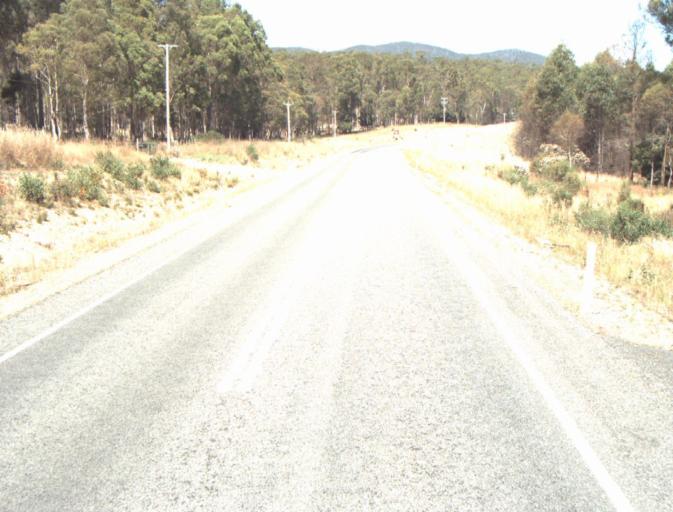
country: AU
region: Tasmania
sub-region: Launceston
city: Newstead
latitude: -41.3372
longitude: 147.3474
